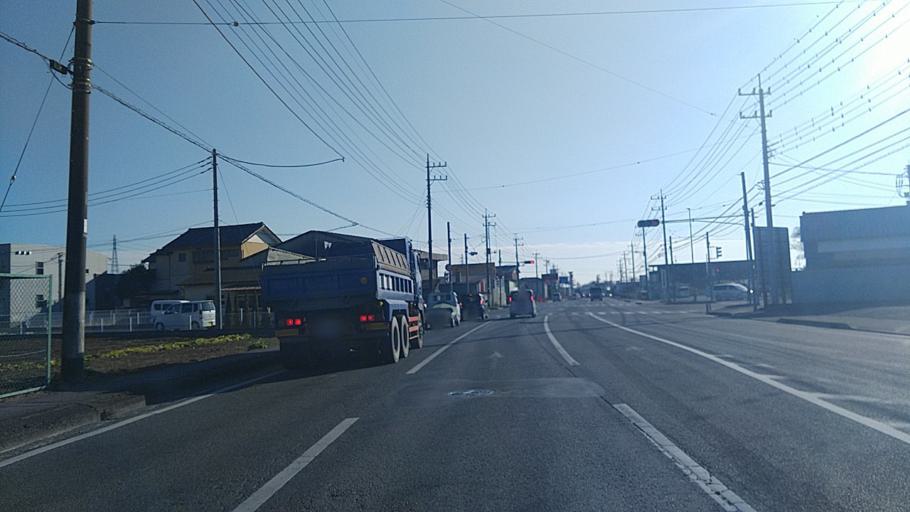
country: JP
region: Tochigi
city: Tanuma
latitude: 36.3617
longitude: 139.5760
